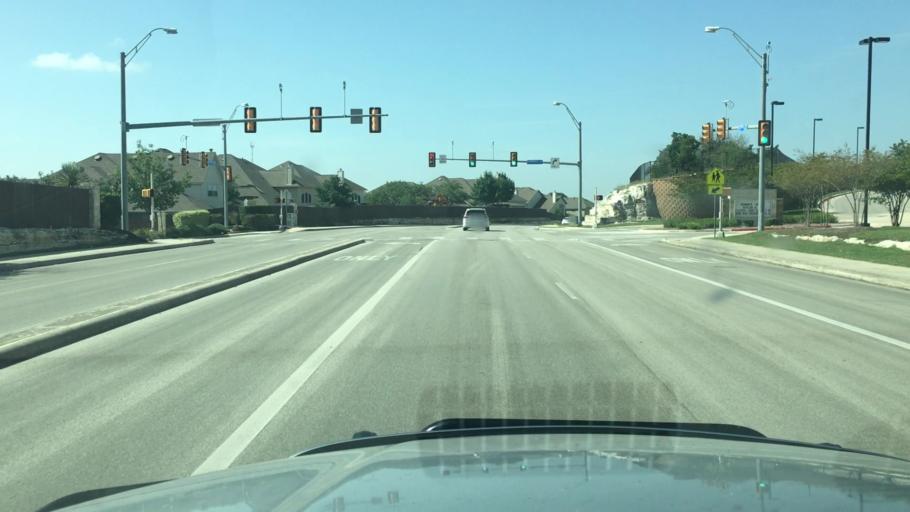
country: US
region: Texas
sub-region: Bexar County
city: Timberwood Park
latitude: 29.6727
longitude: -98.4548
